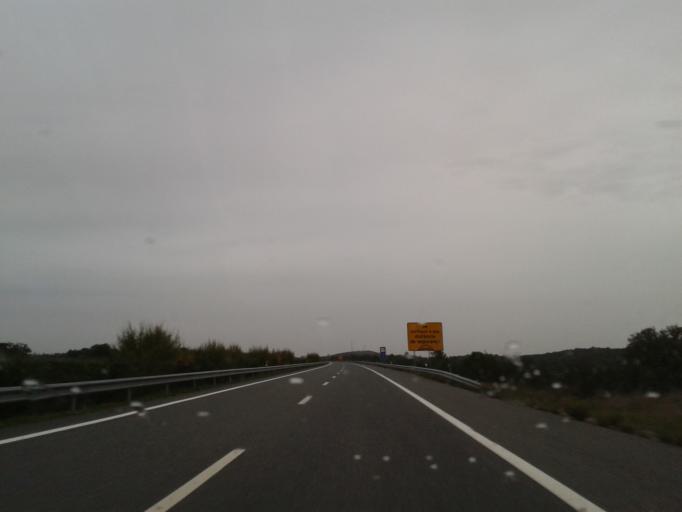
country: PT
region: Beja
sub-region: Ourique
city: Ourique
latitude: 37.6884
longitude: -8.1669
